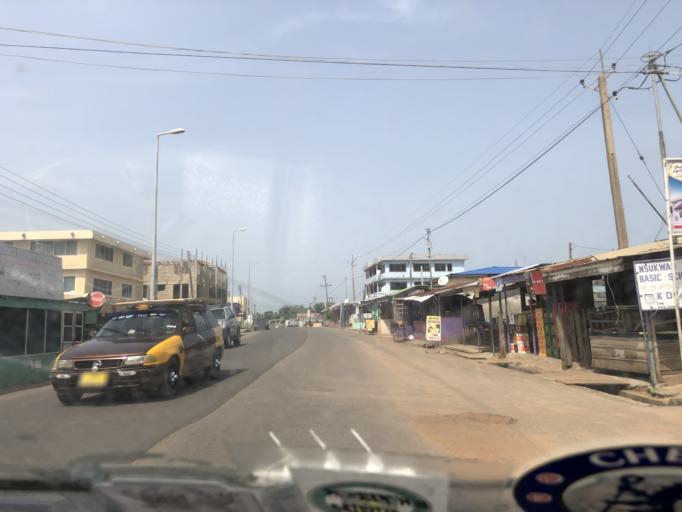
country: GH
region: Eastern
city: Koforidua
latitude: 6.0974
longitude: -0.2654
